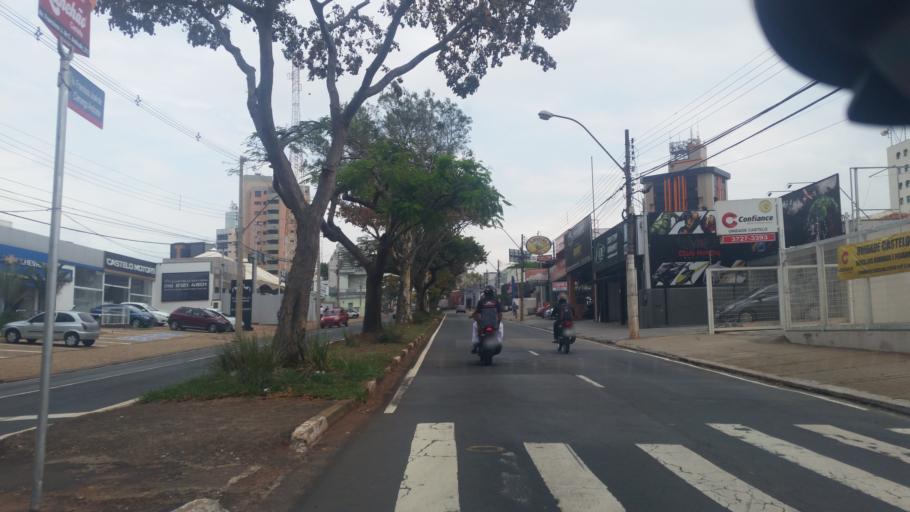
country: BR
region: Sao Paulo
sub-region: Campinas
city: Campinas
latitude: -22.8873
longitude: -47.0759
